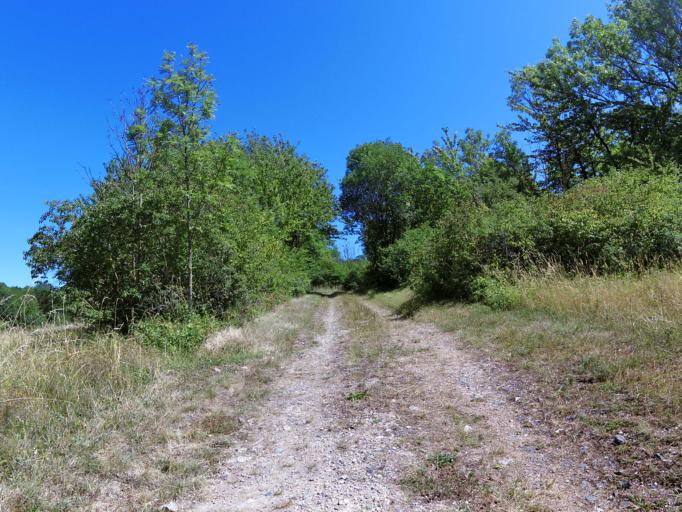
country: DE
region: Bavaria
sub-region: Regierungsbezirk Unterfranken
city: Gerbrunn
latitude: 49.7731
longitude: 10.0064
